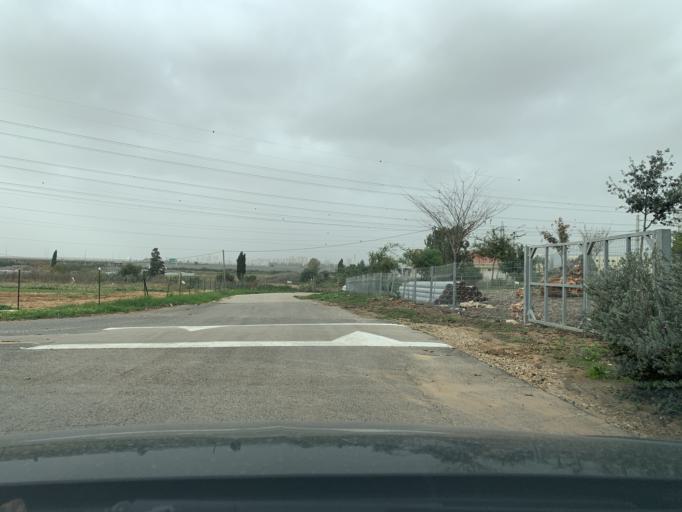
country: IL
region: Central District
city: Jaljulya
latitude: 32.1591
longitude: 34.9393
